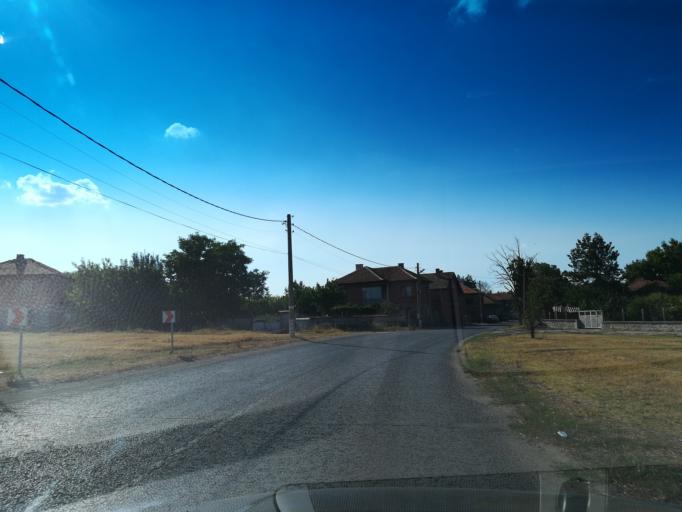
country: BG
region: Khaskovo
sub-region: Obshtina Mineralni Bani
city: Mineralni Bani
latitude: 42.0167
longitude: 25.4202
